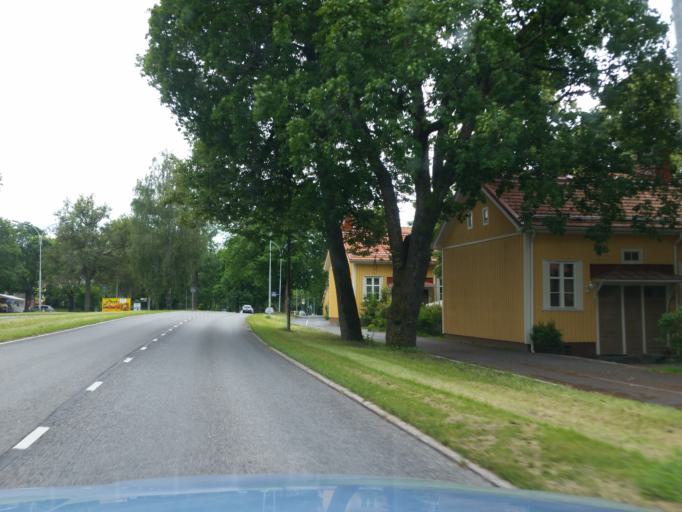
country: FI
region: Varsinais-Suomi
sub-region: Turku
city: Turku
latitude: 60.4397
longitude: 22.2906
